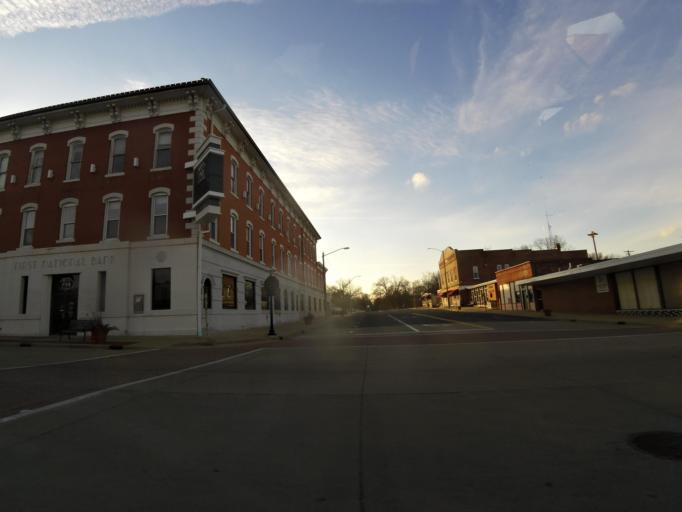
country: US
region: Illinois
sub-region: Fayette County
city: Vandalia
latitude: 38.9607
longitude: -89.0960
